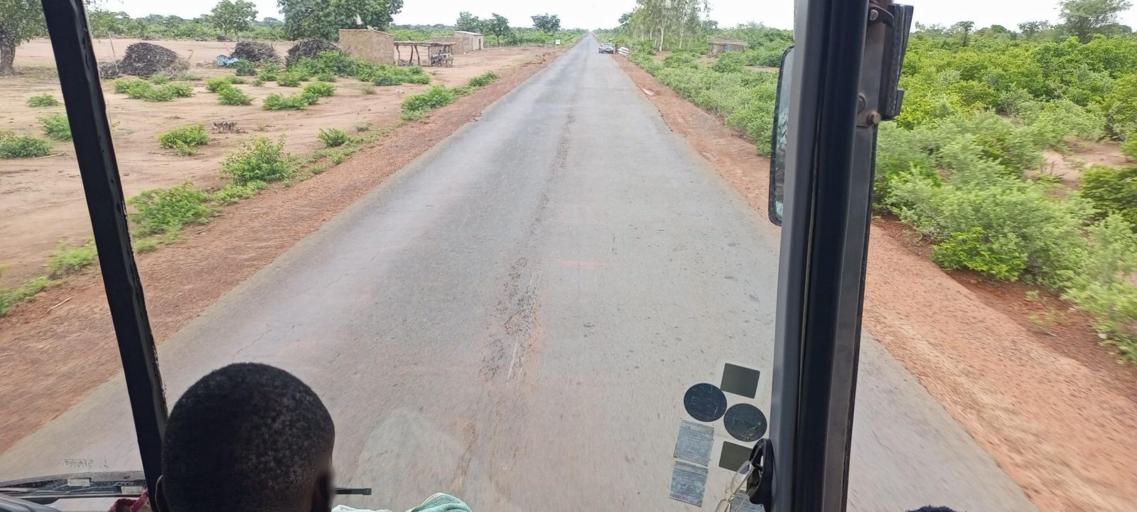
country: ML
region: Sikasso
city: Koutiala
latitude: 12.5570
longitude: -5.5899
